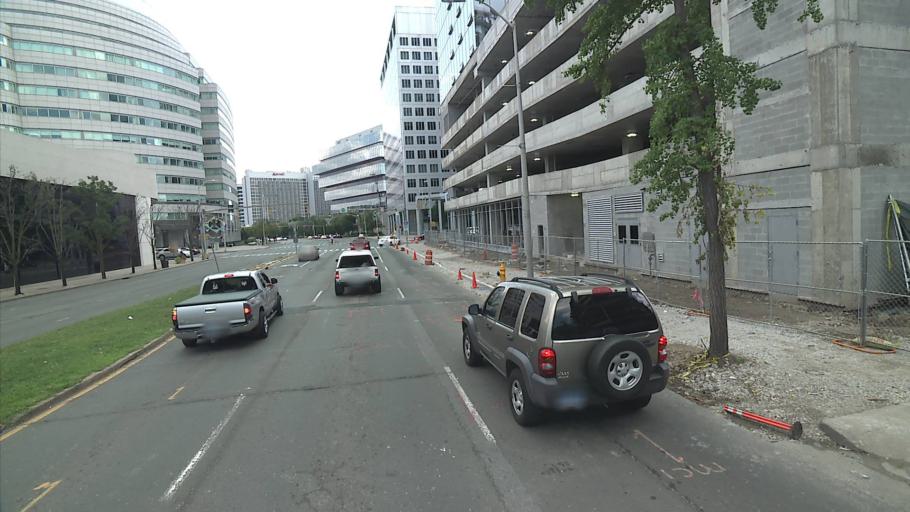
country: US
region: Connecticut
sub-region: Fairfield County
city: Stamford
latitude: 41.0508
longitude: -73.5404
